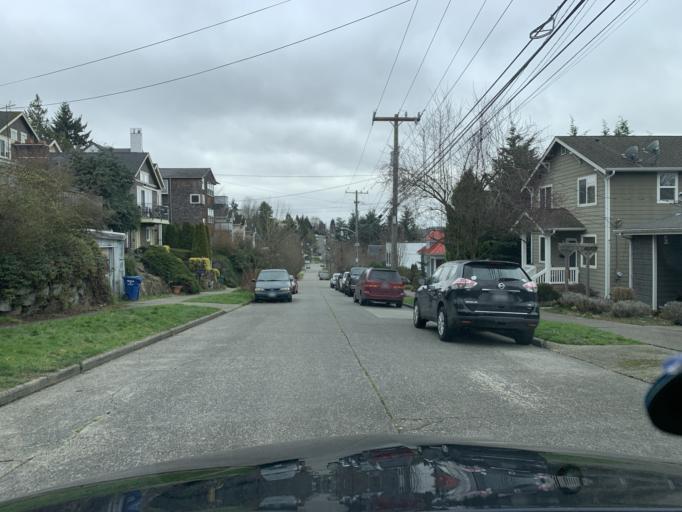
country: US
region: Washington
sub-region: King County
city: Seattle
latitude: 47.5919
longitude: -122.2934
